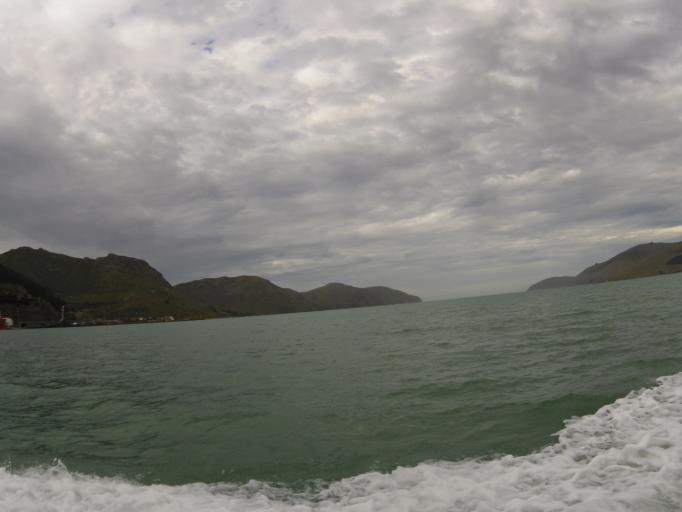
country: NZ
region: Canterbury
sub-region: Christchurch City
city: Christchurch
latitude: -43.6166
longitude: 172.7262
